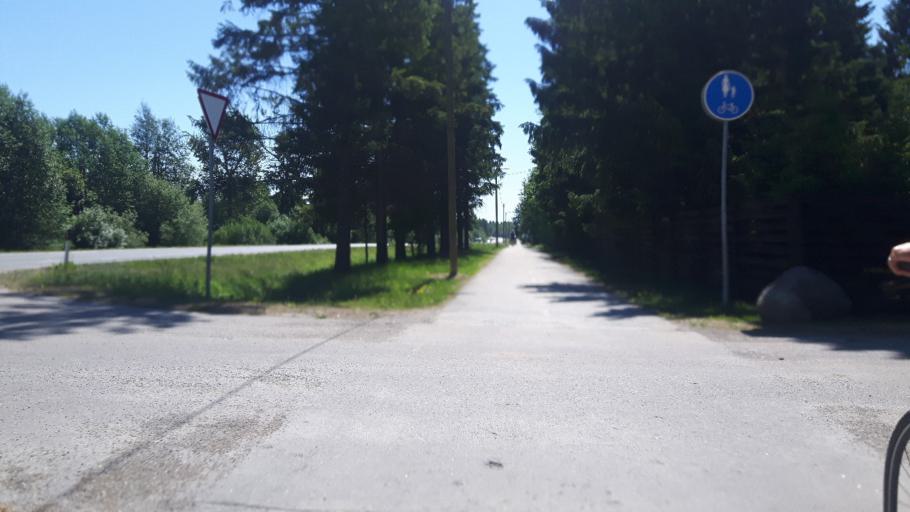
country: EE
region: Harju
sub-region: Saku vald
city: Saku
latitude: 59.2847
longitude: 24.6631
